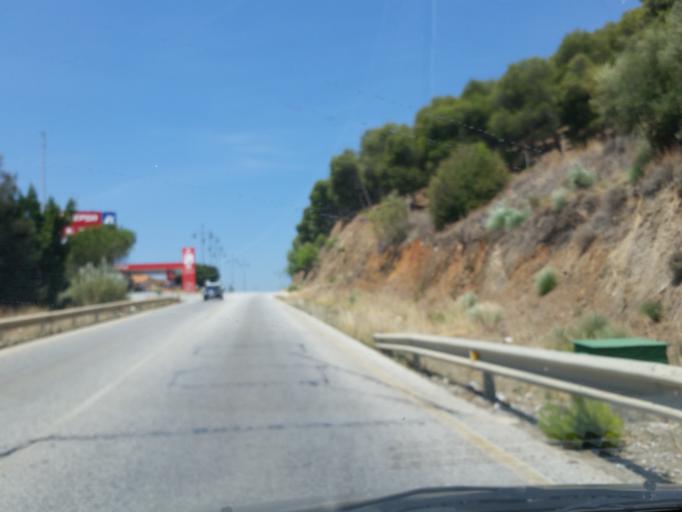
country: ES
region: Andalusia
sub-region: Provincia de Malaga
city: Benalmadena
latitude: 36.5875
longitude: -4.5974
